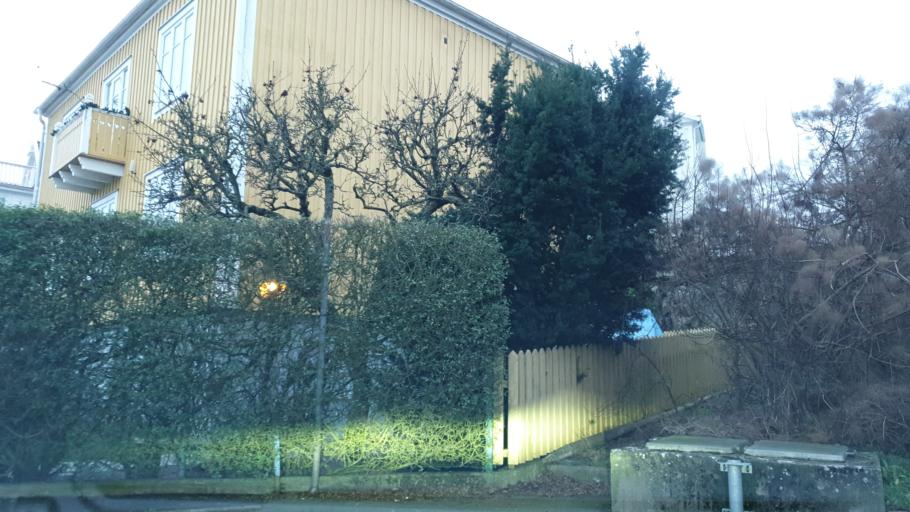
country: SE
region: Blekinge
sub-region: Karlskrona Kommun
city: Karlskrona
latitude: 56.1654
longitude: 15.5741
